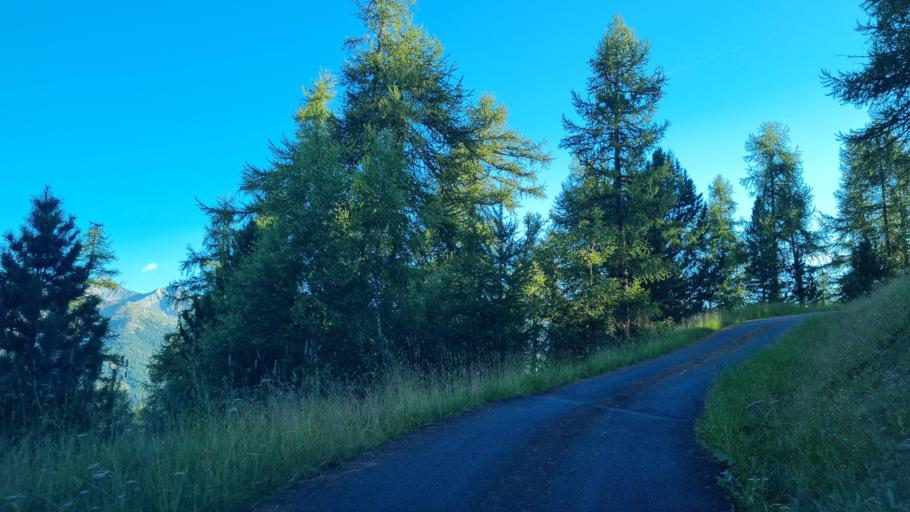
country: IT
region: Aosta Valley
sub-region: Valle d'Aosta
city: Fontainemore
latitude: 45.6262
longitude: 7.8734
